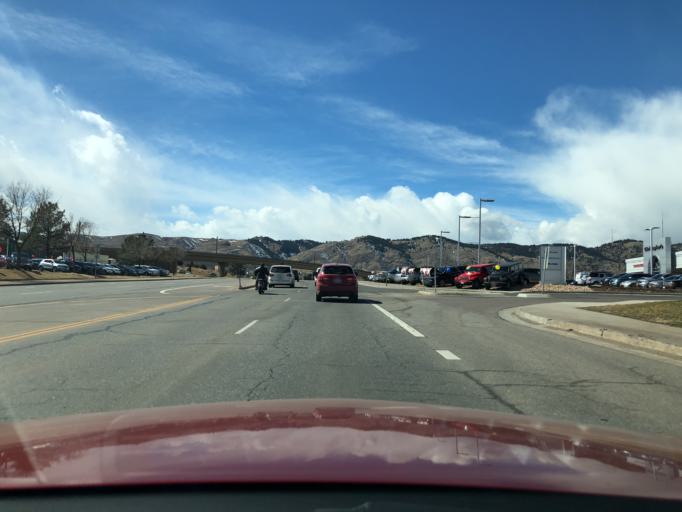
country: US
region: Colorado
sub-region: Jefferson County
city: West Pleasant View
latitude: 39.7270
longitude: -105.1851
